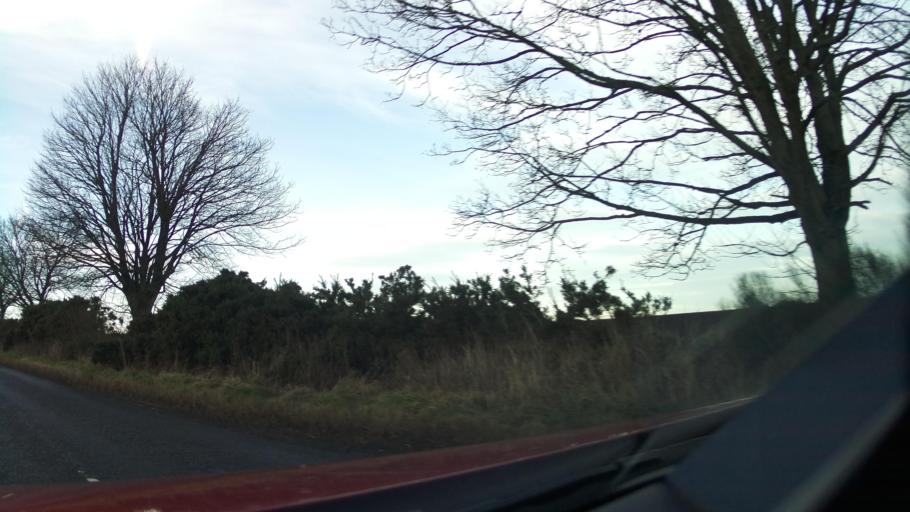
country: GB
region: Scotland
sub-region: Angus
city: Letham
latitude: 56.5568
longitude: -2.7653
